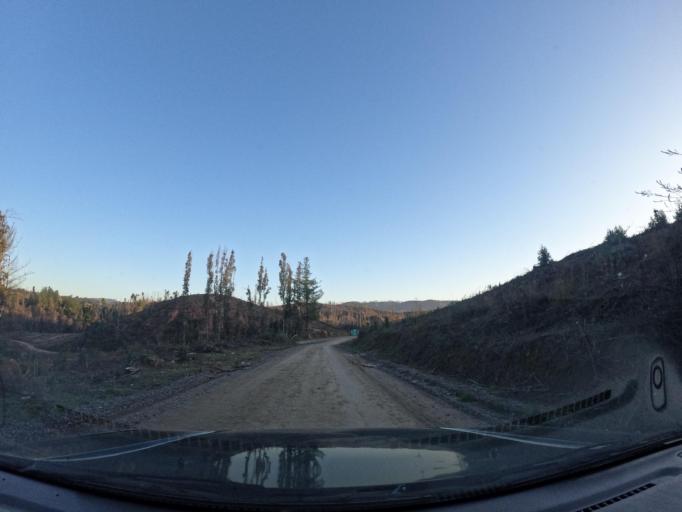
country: CL
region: Biobio
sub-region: Provincia de Concepcion
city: Chiguayante
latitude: -37.0114
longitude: -72.8957
